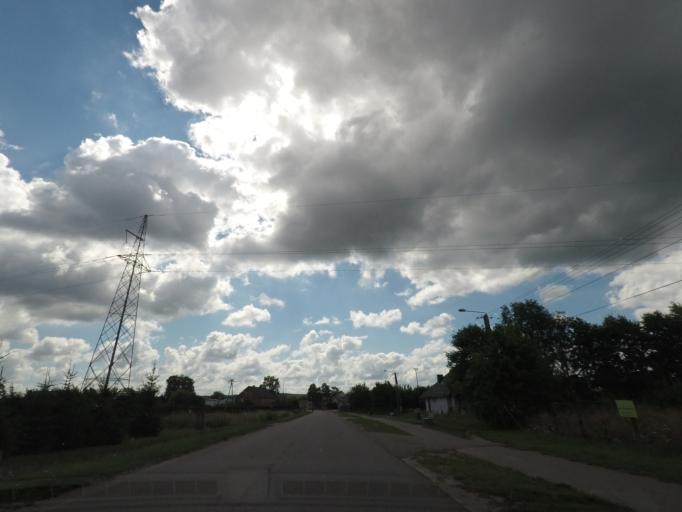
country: PL
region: Pomeranian Voivodeship
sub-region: Powiat wejherowski
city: Leczyce
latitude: 54.5867
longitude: 17.8615
